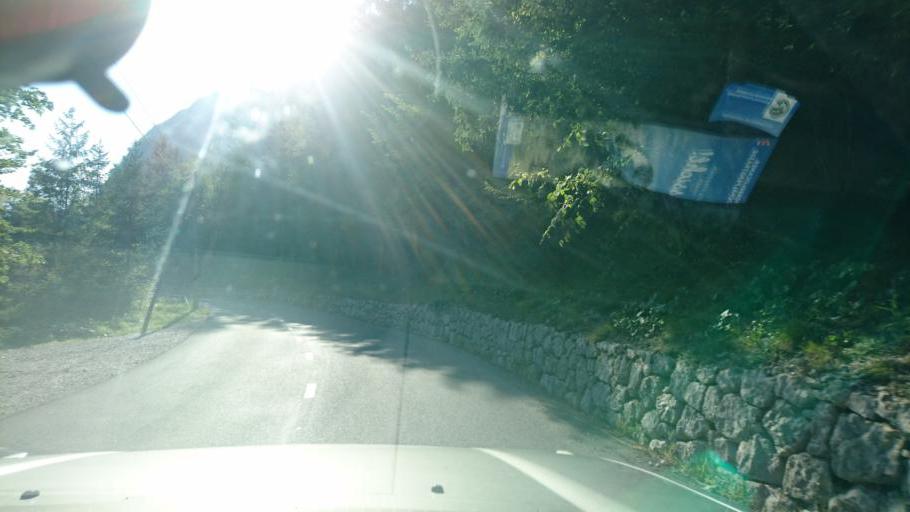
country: SI
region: Kranjska Gora
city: Kranjska Gora
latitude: 46.3708
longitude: 13.7296
